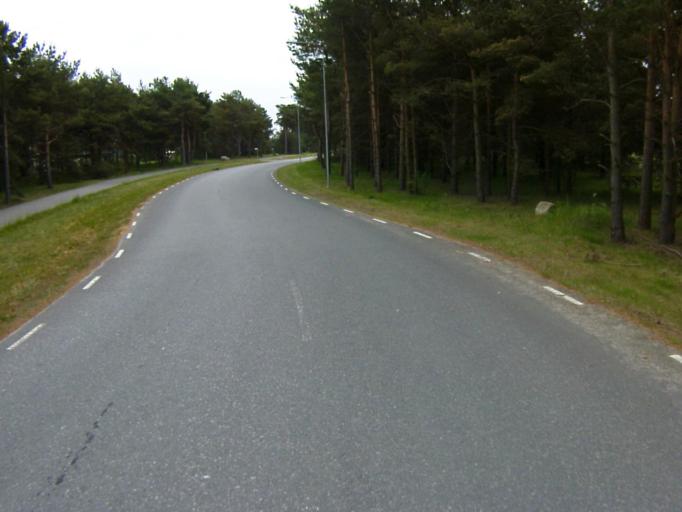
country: SE
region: Skane
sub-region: Kristianstads Kommun
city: Ahus
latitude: 55.9363
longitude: 14.2673
